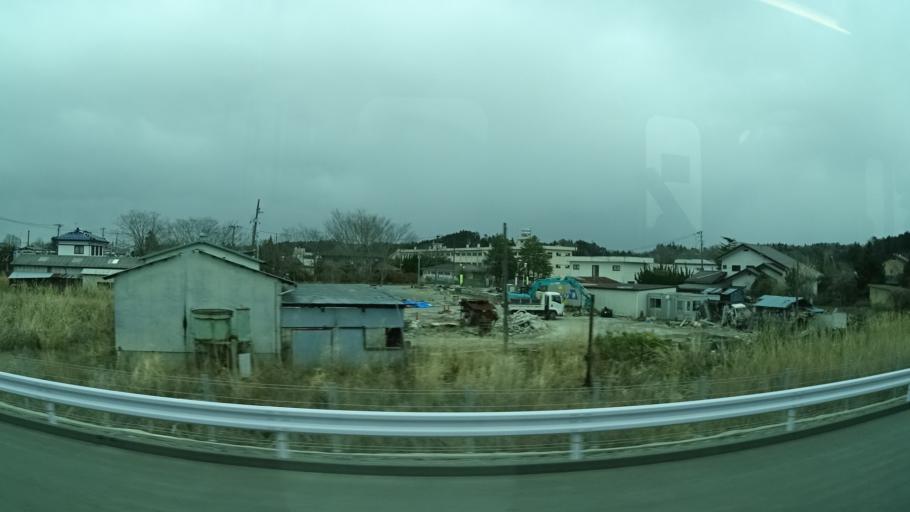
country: JP
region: Fukushima
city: Namie
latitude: 37.4463
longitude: 141.0035
